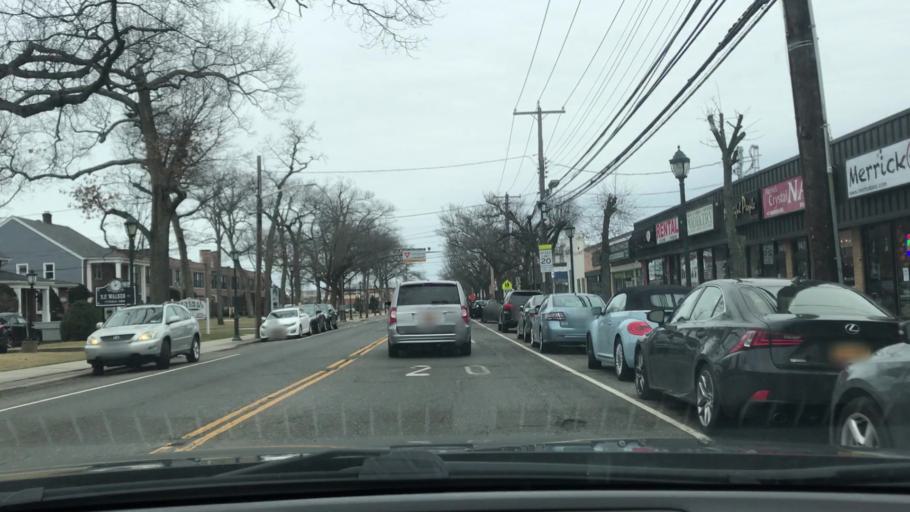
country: US
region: New York
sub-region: Nassau County
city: Merrick
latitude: 40.6684
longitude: -73.5542
